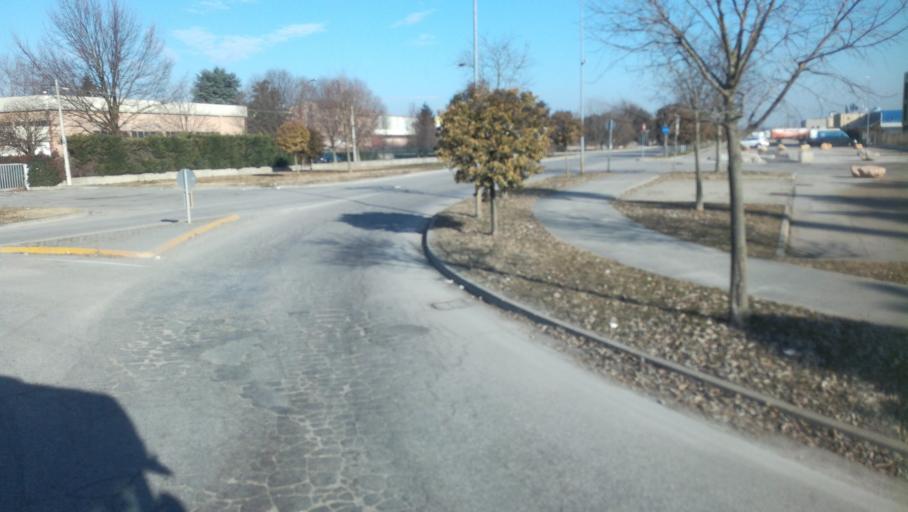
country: IT
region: Veneto
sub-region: Provincia di Verona
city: Pradelle
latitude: 45.2762
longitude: 10.8589
